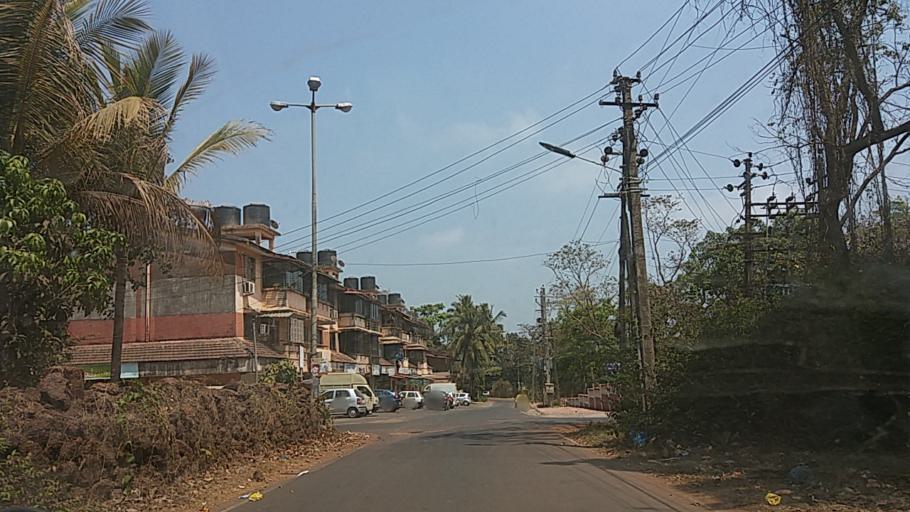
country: IN
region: Goa
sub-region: North Goa
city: Panaji
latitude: 15.5157
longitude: 73.8371
